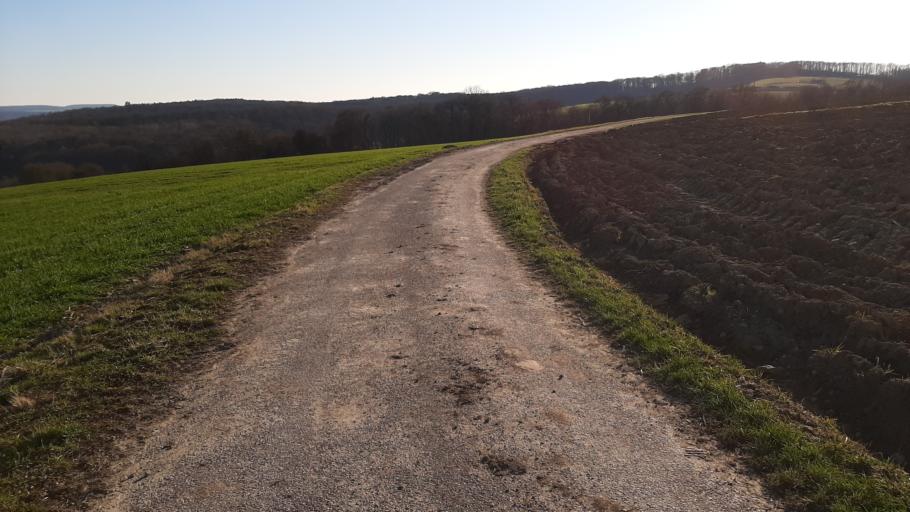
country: LU
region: Grevenmacher
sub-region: Canton d'Echternach
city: Mompach
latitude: 49.7477
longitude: 6.4903
